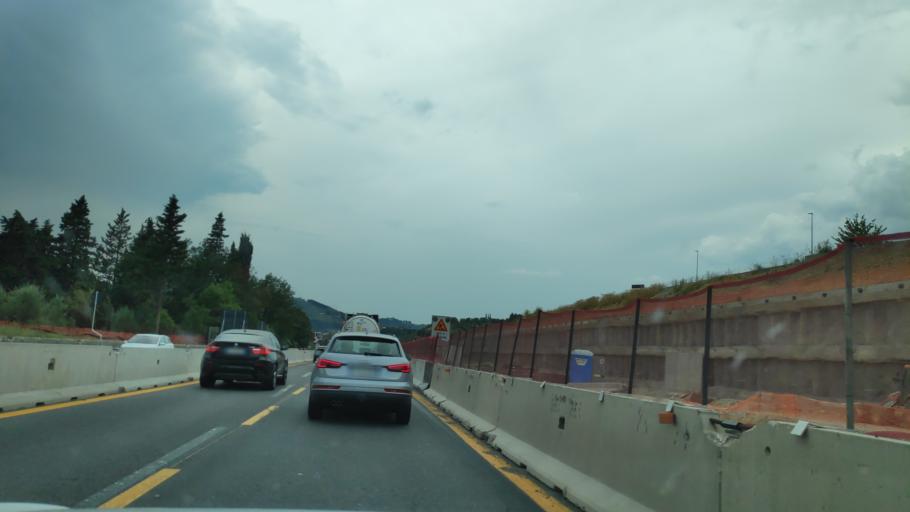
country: IT
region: Tuscany
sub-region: Province of Florence
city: Antella
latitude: 43.7303
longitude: 11.3200
